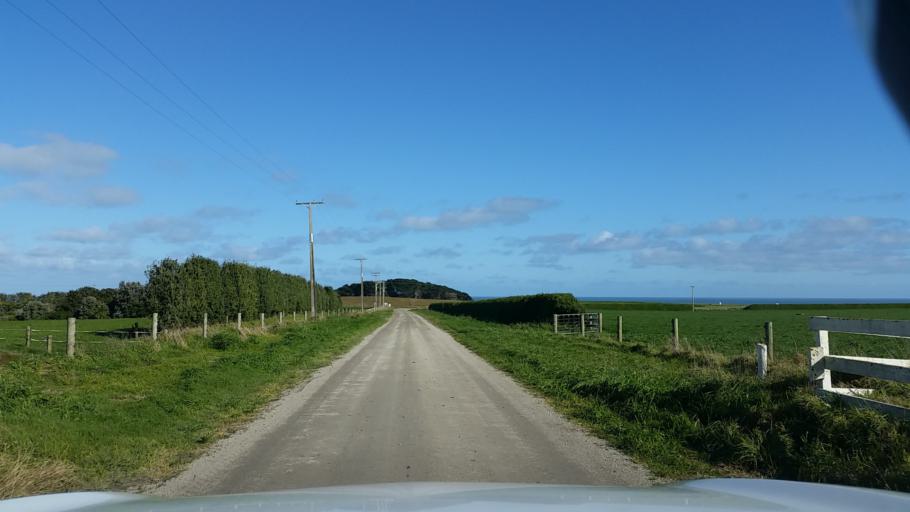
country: NZ
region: Taranaki
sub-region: South Taranaki District
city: Patea
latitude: -39.6853
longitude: 174.3988
